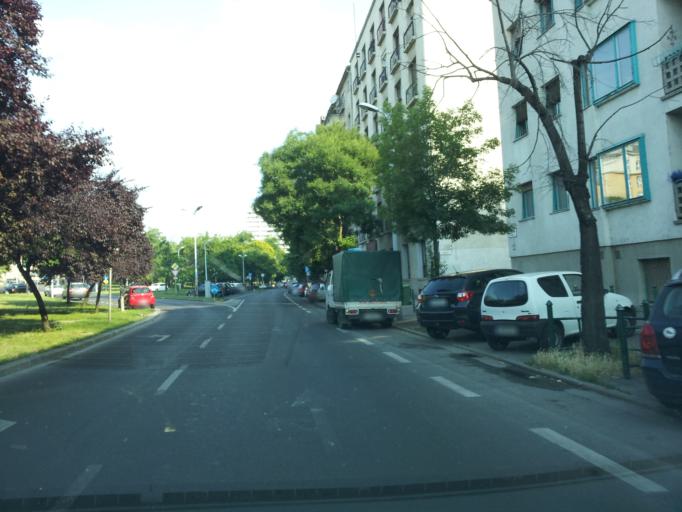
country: HU
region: Budapest
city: Budapest I. keruelet
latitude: 47.4948
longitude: 19.0372
